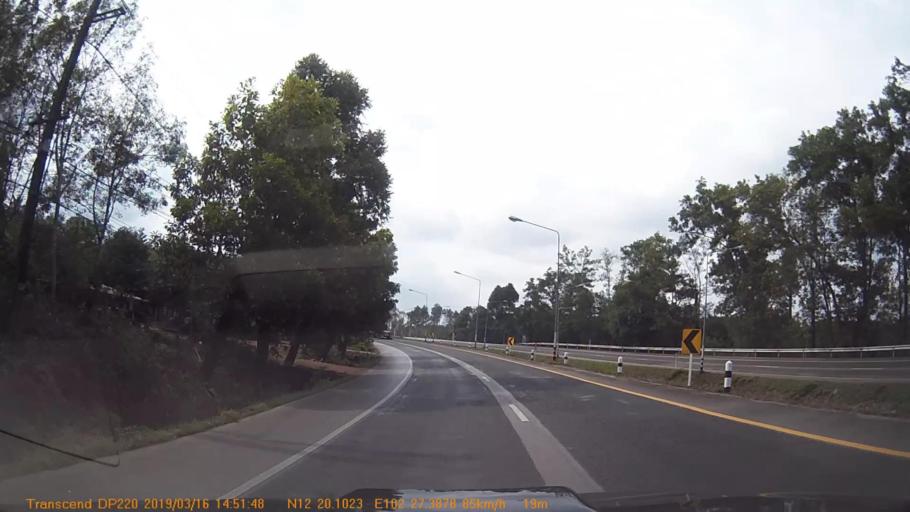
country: TH
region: Trat
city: Khao Saming
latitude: 12.3354
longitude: 102.4562
